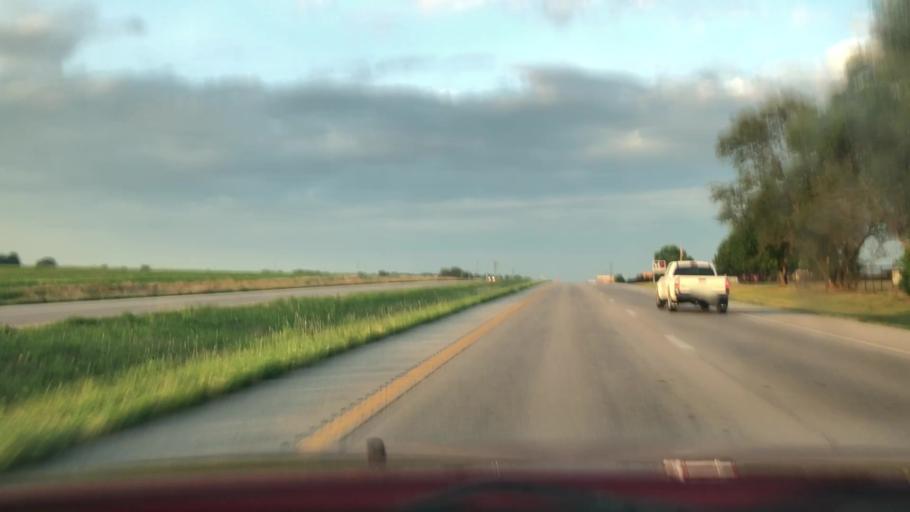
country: US
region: Missouri
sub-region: Greene County
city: Battlefield
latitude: 37.1509
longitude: -93.4190
